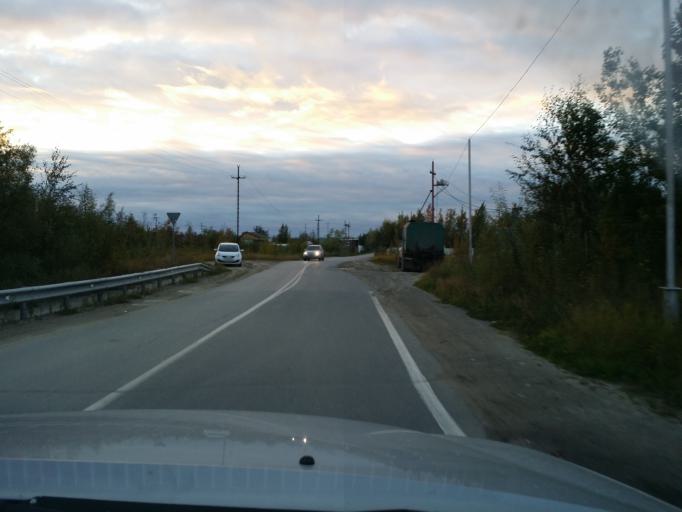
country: RU
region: Khanty-Mansiyskiy Avtonomnyy Okrug
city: Megion
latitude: 61.0639
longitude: 76.1857
